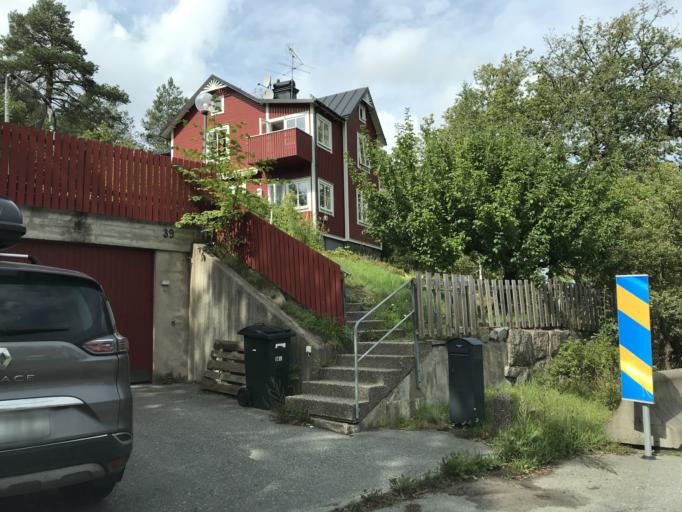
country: SE
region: Stockholm
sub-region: Sundbybergs Kommun
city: Sundbyberg
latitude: 59.3382
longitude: 17.9748
